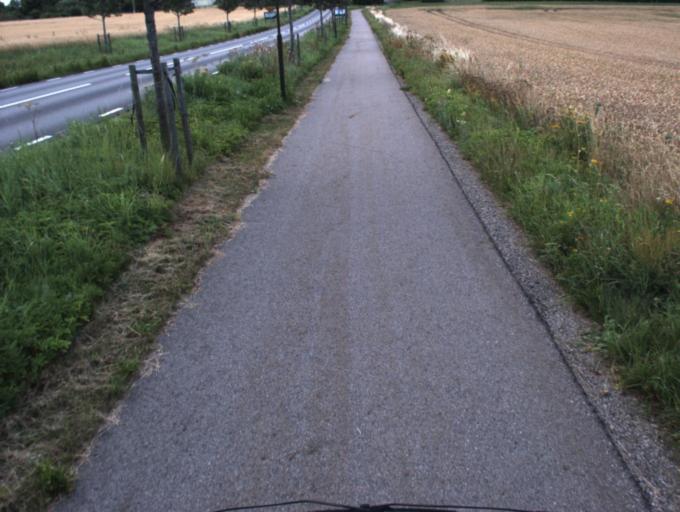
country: SE
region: Skane
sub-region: Helsingborg
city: Helsingborg
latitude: 56.0997
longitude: 12.6491
